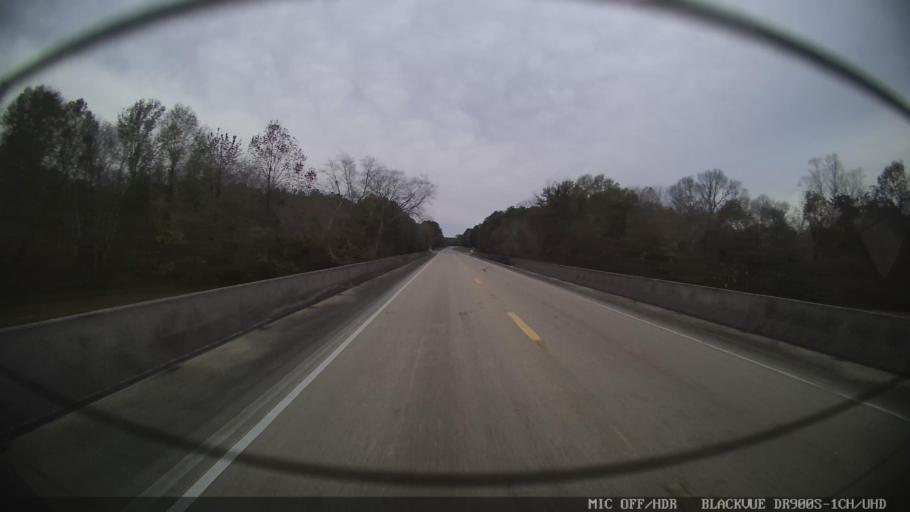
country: US
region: Mississippi
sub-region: Clarke County
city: Quitman
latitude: 32.0267
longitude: -88.8377
